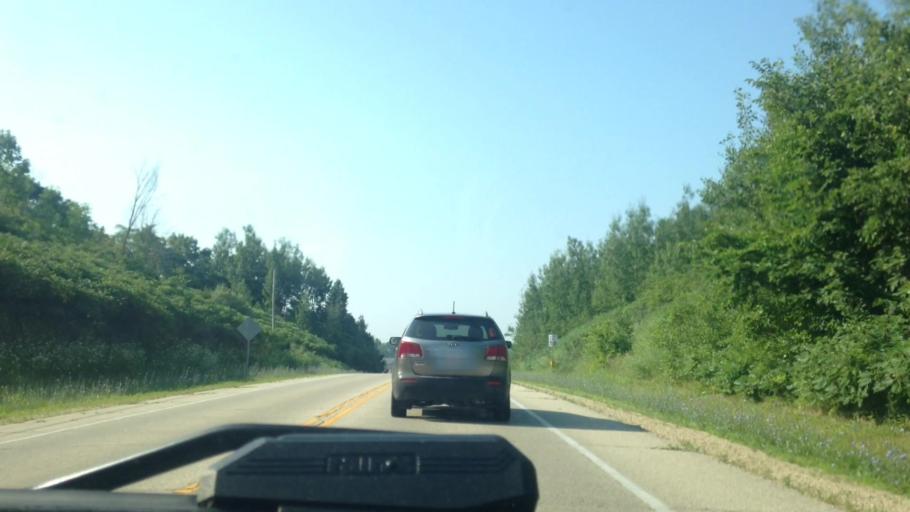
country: US
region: Wisconsin
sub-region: Waukesha County
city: Merton
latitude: 43.1999
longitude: -88.2615
